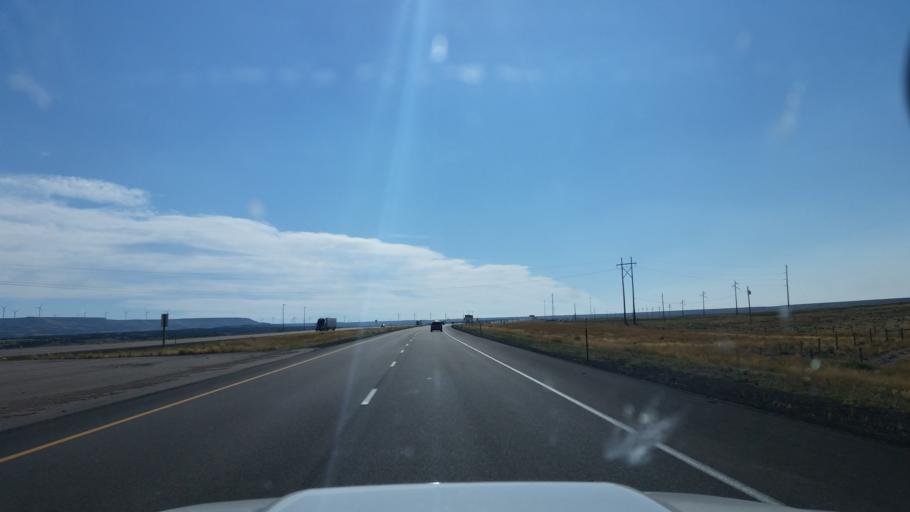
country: US
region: Wyoming
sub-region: Uinta County
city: Mountain View
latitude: 41.3341
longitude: -110.4188
